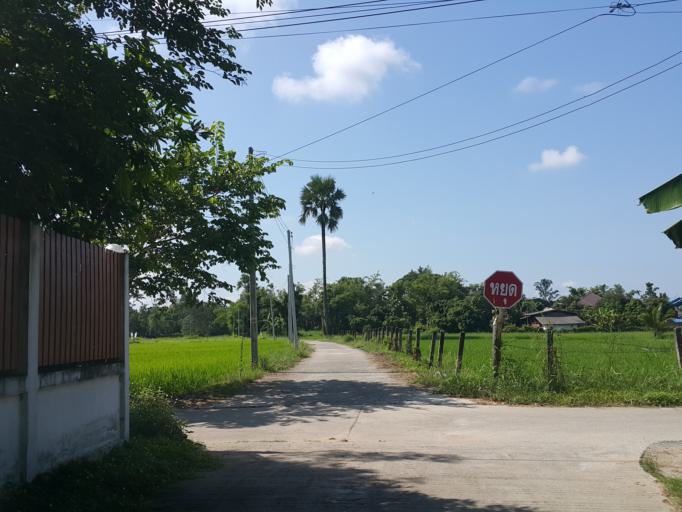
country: TH
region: Chiang Mai
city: San Kamphaeng
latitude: 18.7634
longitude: 99.1732
